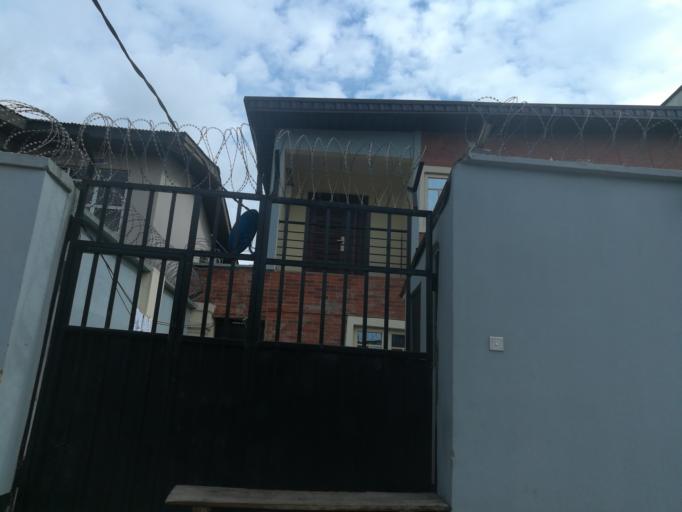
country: NG
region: Lagos
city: Somolu
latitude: 6.5479
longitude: 3.3686
